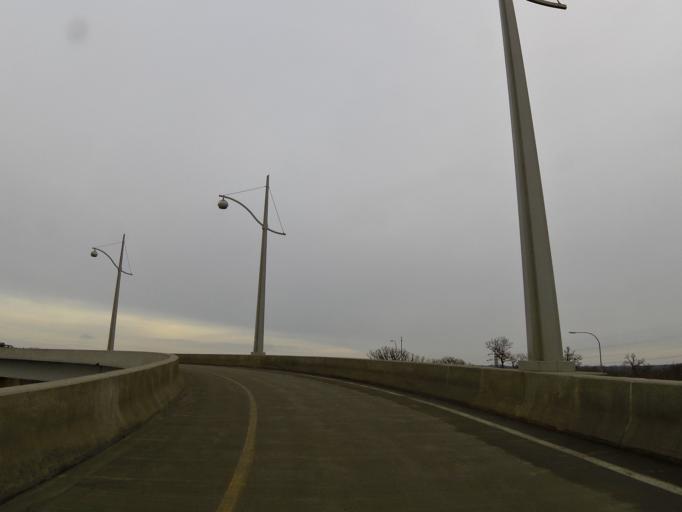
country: US
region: Minnesota
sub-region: Dakota County
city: Mendota Heights
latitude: 44.8774
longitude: -93.1957
